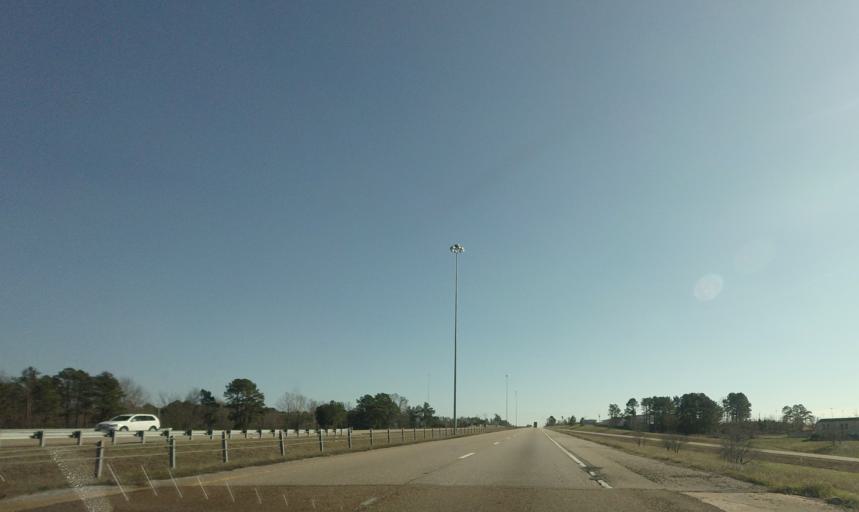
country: US
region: Mississippi
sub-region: Marshall County
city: Holly Springs
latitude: 34.7472
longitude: -89.4541
